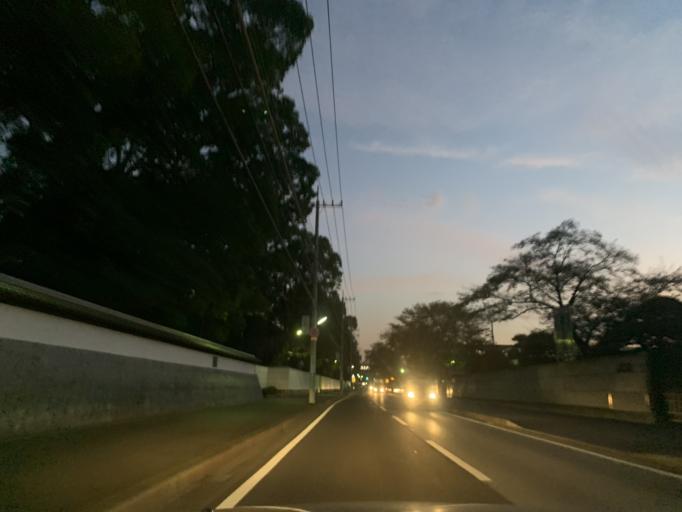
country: JP
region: Chiba
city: Noda
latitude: 35.9220
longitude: 139.9073
